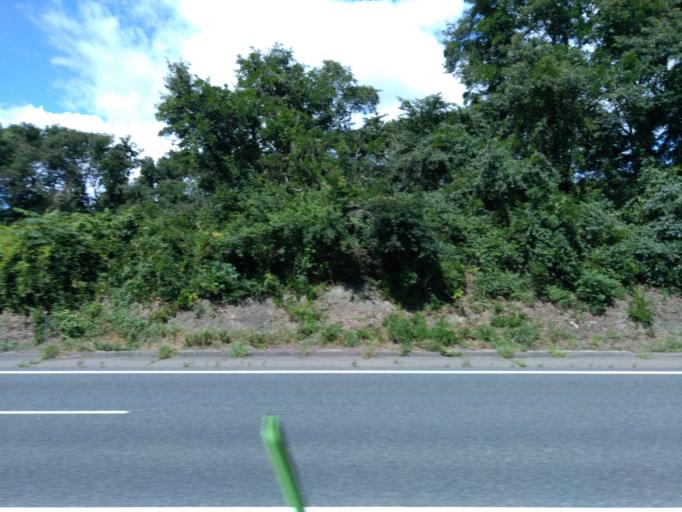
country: JP
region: Miyagi
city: Tomiya
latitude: 38.4012
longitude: 140.9059
